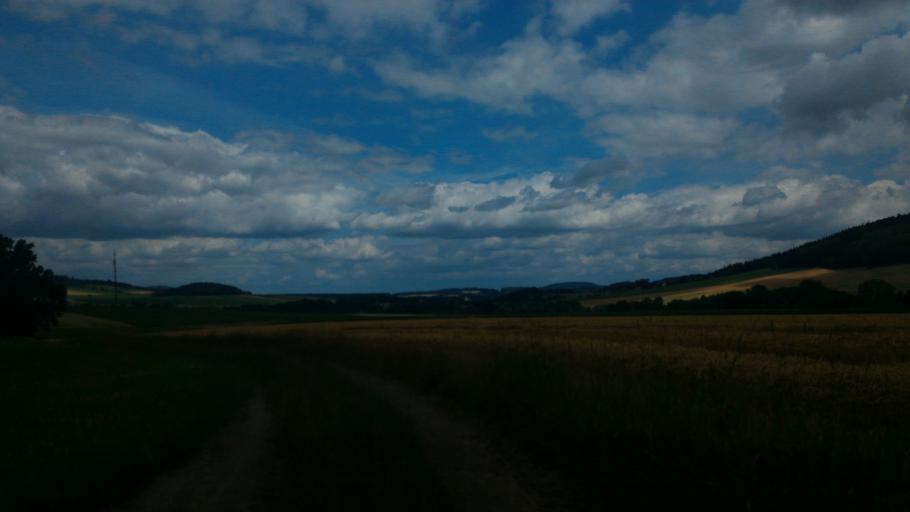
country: DE
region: Saxony
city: Grossschonau
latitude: 50.8823
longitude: 14.6799
